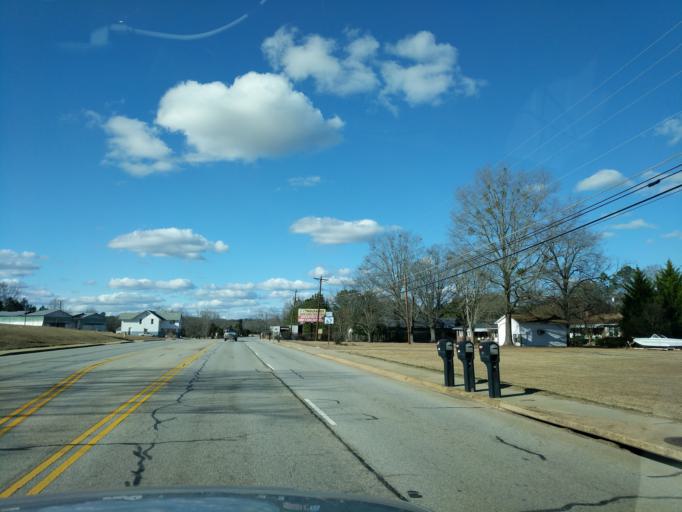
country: US
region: South Carolina
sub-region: Greenwood County
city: Greenwood
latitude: 34.1280
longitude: -82.1233
